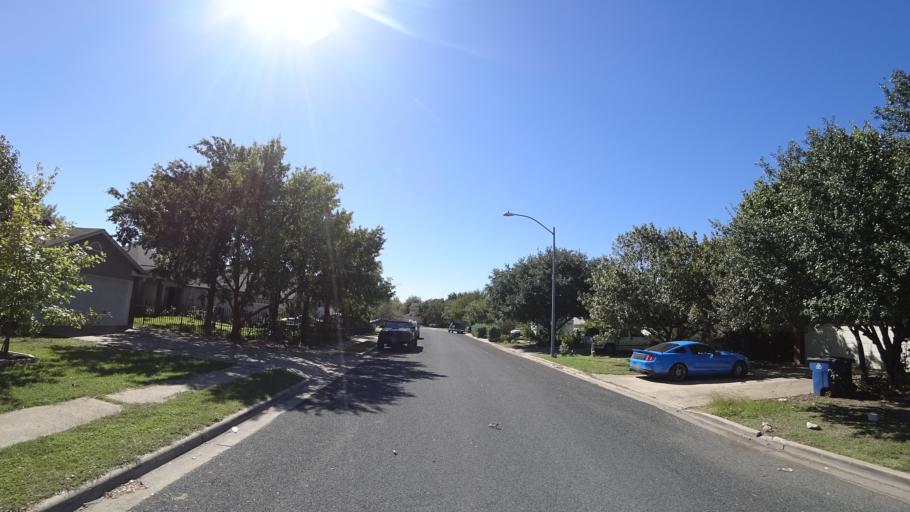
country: US
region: Texas
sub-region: Travis County
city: Hornsby Bend
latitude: 30.3060
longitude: -97.6411
